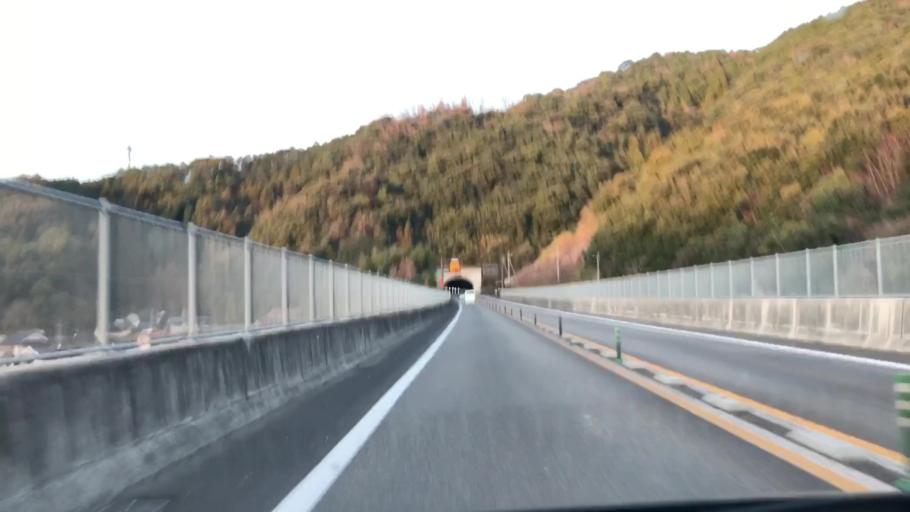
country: JP
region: Kumamoto
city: Minamata
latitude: 32.3016
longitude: 130.5105
